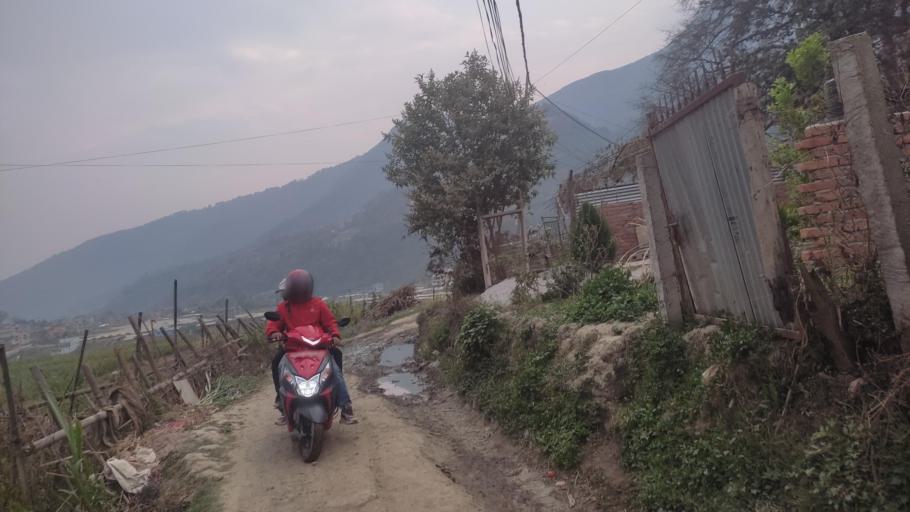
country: NP
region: Central Region
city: Kirtipur
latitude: 27.6635
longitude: 85.2728
